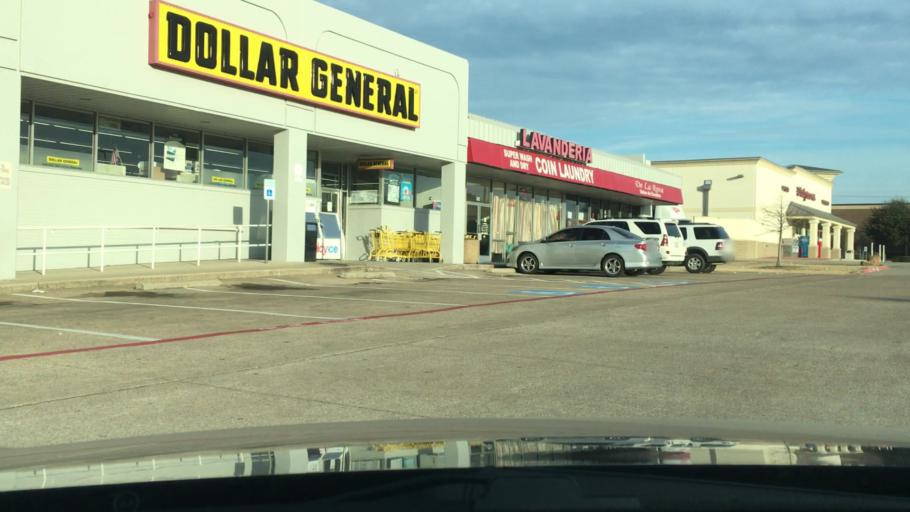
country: US
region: Texas
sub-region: Collin County
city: Plano
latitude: 33.0299
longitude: -96.6833
